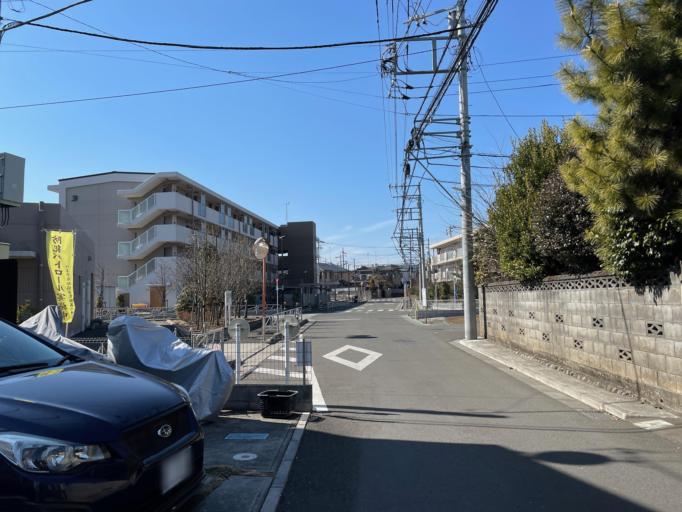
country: JP
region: Tokyo
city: Hachioji
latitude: 35.6729
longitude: 139.3195
